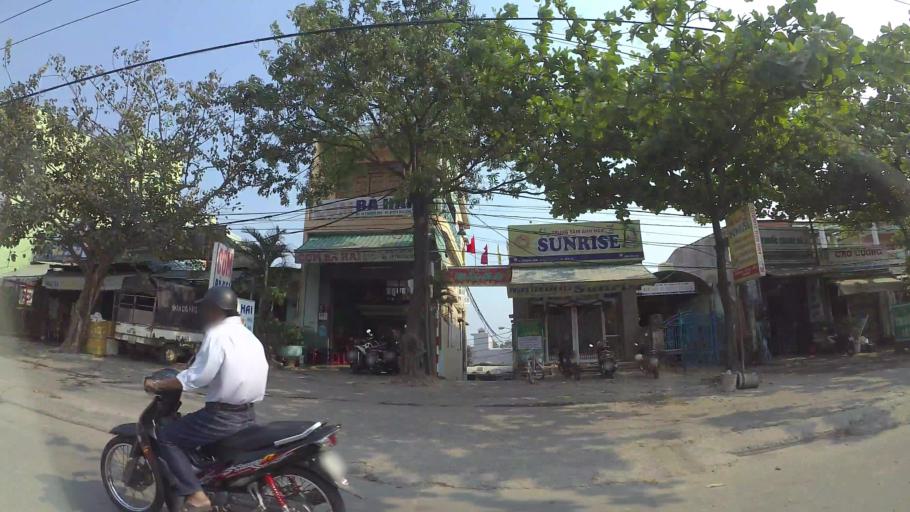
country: VN
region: Da Nang
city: Cam Le
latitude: 16.0120
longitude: 108.1878
